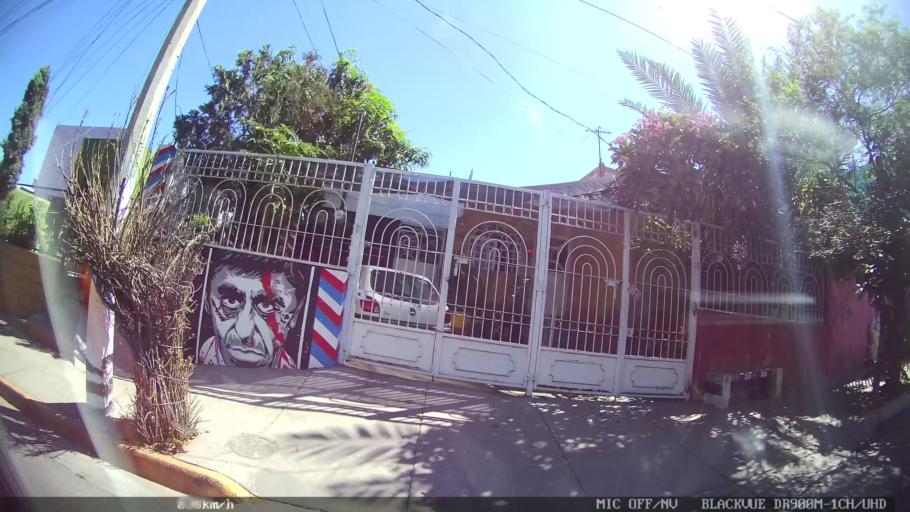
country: MX
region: Jalisco
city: Tlaquepaque
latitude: 20.6885
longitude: -103.2787
